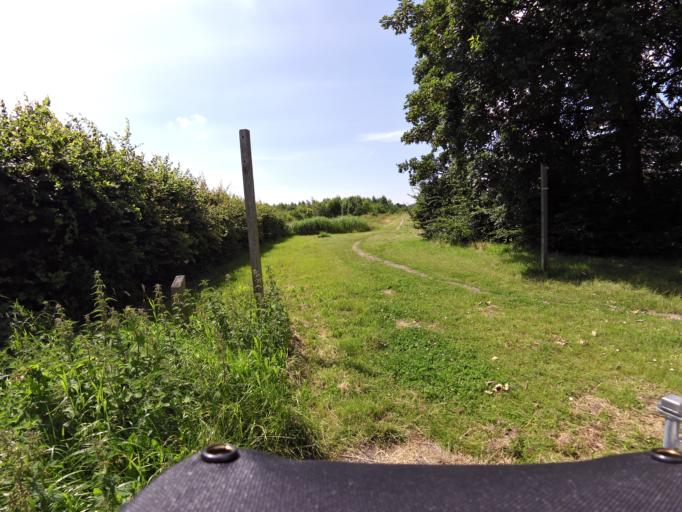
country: NL
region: South Holland
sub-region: Gemeente Albrandswaard
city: Rhoon
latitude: 51.8665
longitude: 4.4317
